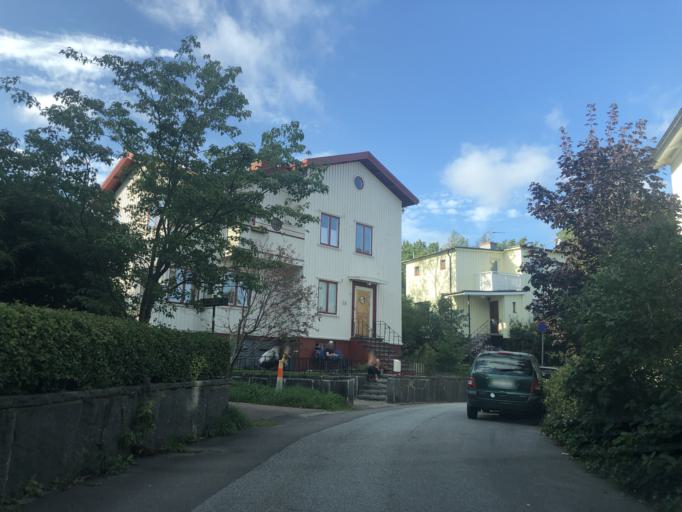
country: SE
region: Vaestra Goetaland
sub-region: Goteborg
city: Majorna
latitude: 57.6800
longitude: 11.9242
